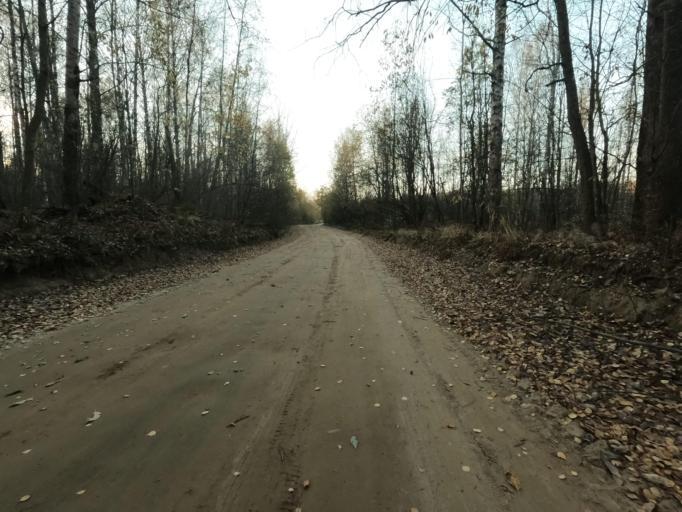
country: RU
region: Leningrad
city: Mga
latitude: 59.7551
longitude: 31.2799
